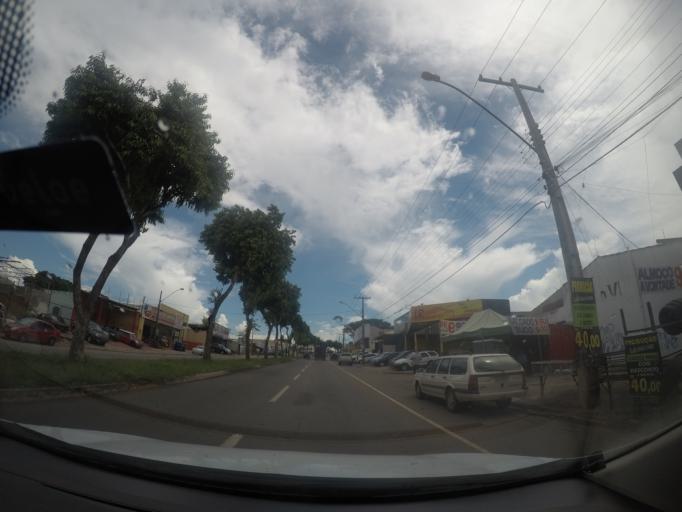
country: BR
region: Goias
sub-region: Goiania
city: Goiania
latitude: -16.7470
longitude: -49.3310
